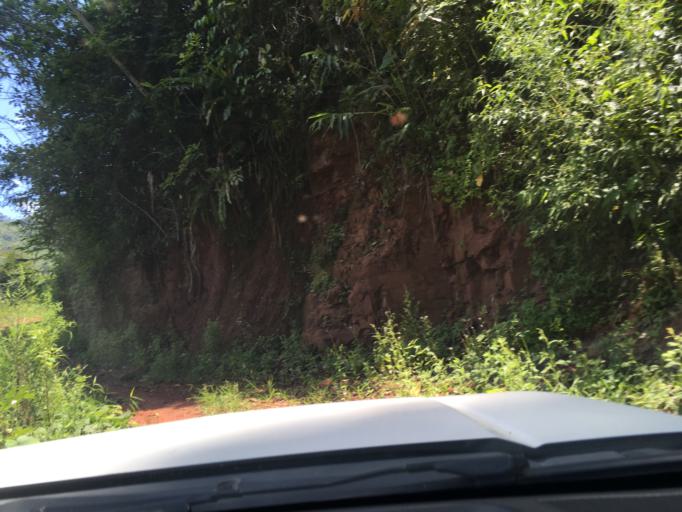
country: LA
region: Phongsali
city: Phongsali
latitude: 21.7905
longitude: 101.8644
